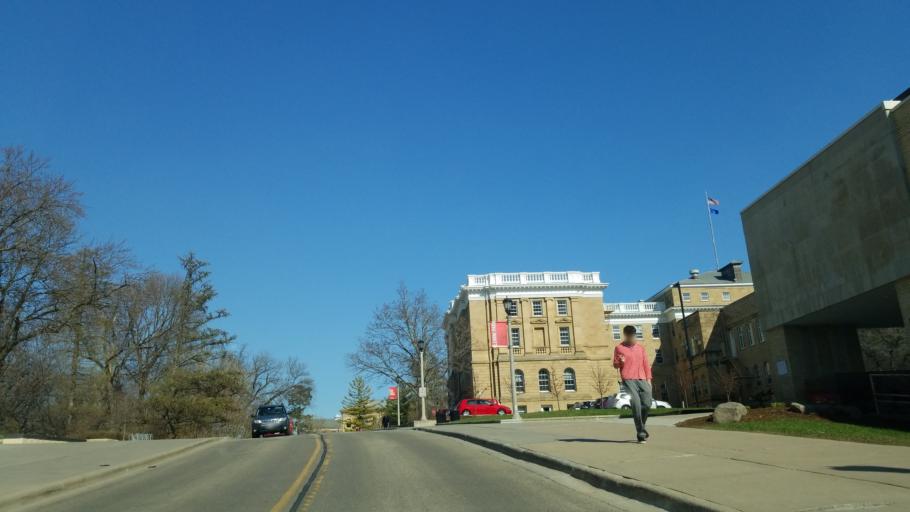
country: US
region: Wisconsin
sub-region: Dane County
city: Madison
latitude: 43.0760
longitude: -89.4054
